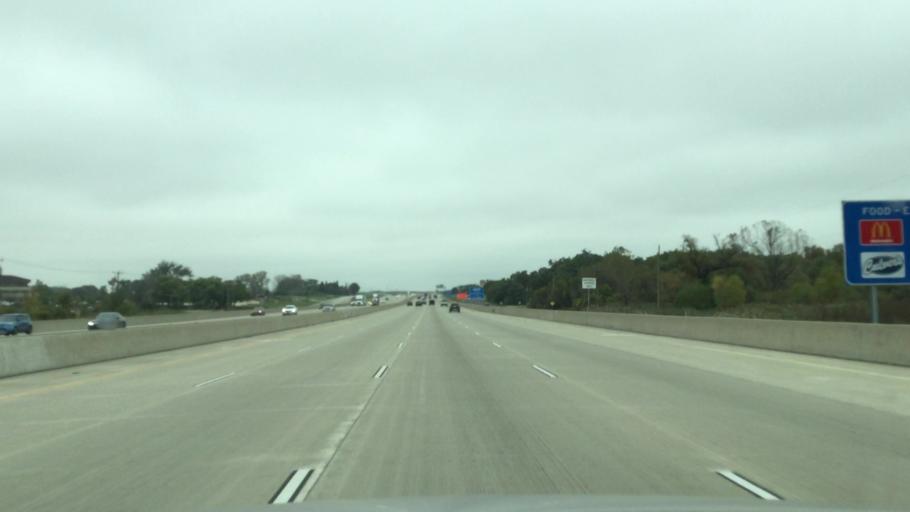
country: US
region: Wisconsin
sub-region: Kenosha County
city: Pleasant Prairie
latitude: 42.5098
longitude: -87.9515
